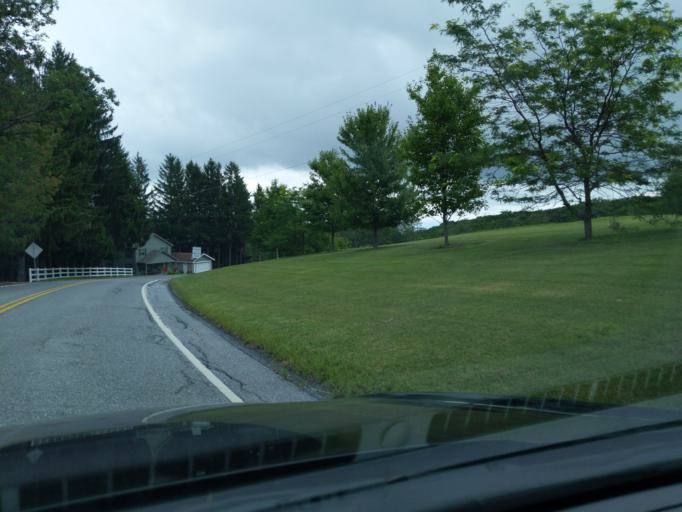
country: US
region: Pennsylvania
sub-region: Cambria County
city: Cresson
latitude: 40.3566
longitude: -78.5528
